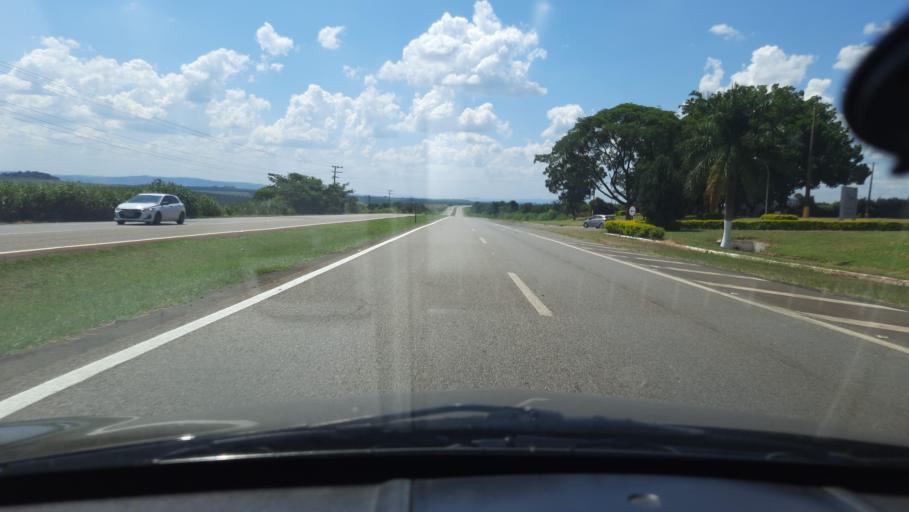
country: BR
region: Sao Paulo
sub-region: Casa Branca
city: Casa Branca
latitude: -21.7198
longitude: -47.0804
